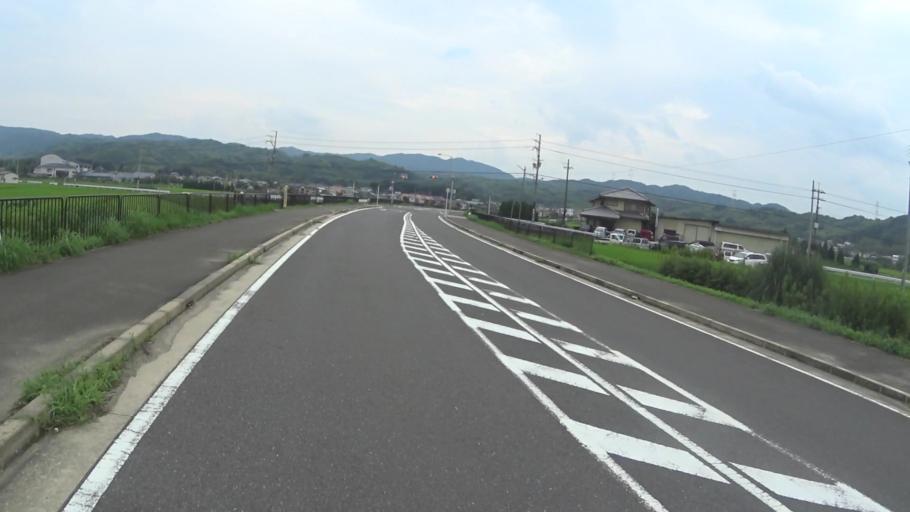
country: JP
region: Kyoto
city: Tanabe
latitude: 34.7724
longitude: 135.8096
